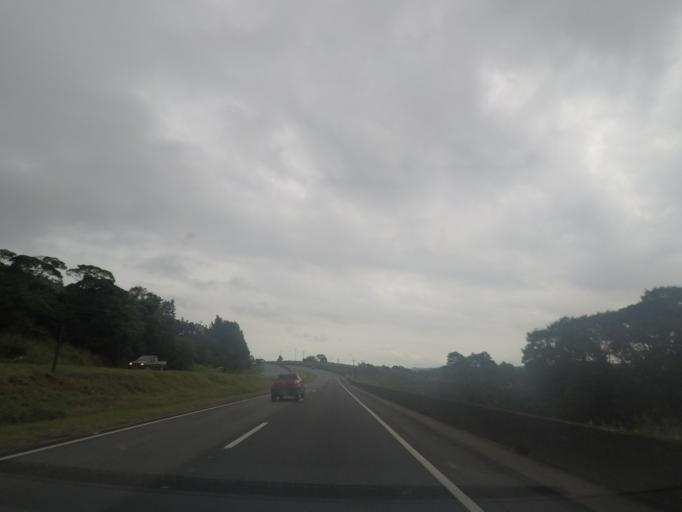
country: BR
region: Parana
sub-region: Campina Grande Do Sul
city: Campina Grande do Sul
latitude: -25.1523
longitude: -48.8601
